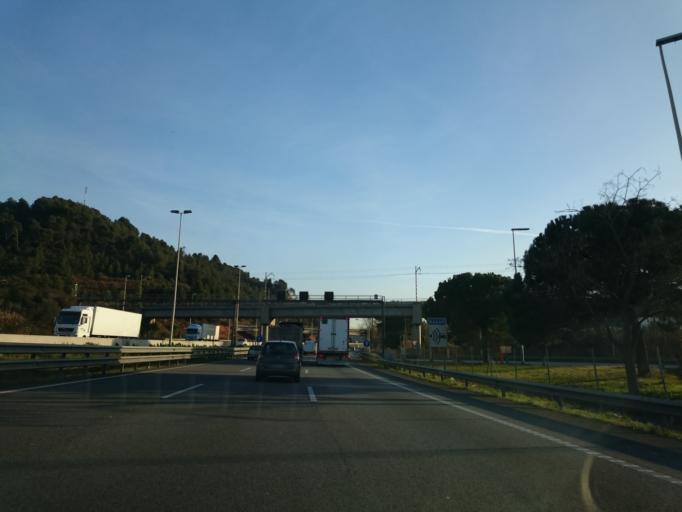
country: ES
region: Catalonia
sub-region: Provincia de Barcelona
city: Castellbisbal
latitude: 41.4648
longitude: 1.9795
